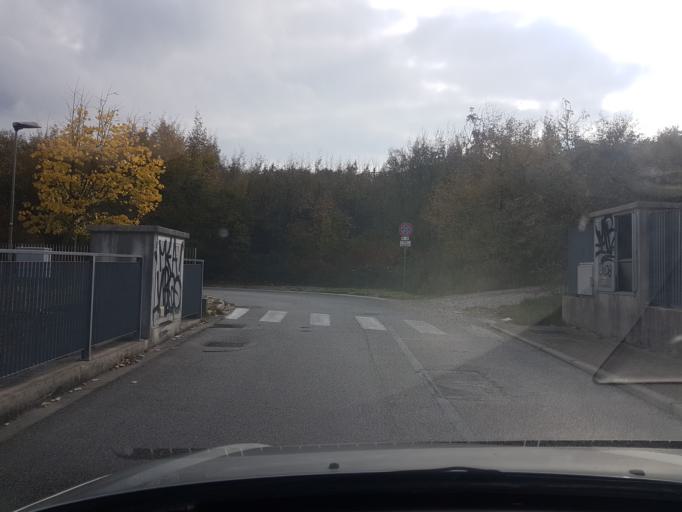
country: IT
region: Friuli Venezia Giulia
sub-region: Provincia di Trieste
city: Aurisina Cave
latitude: 45.7550
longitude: 13.6531
